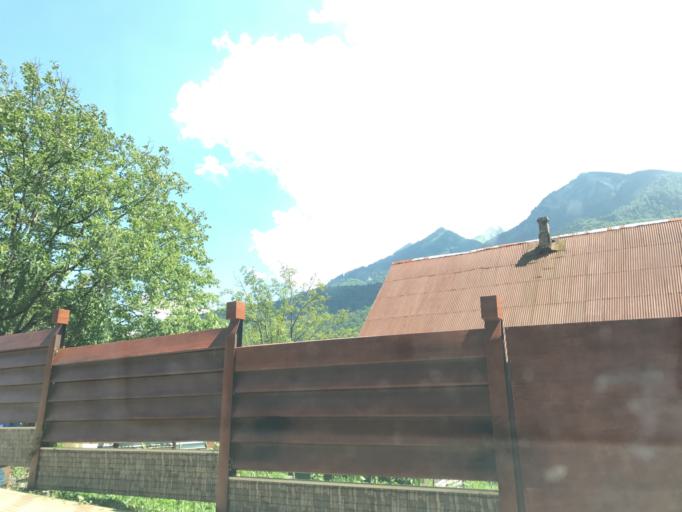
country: RU
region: Krasnodarskiy
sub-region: Sochi City
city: Krasnaya Polyana
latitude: 43.6768
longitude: 40.2028
